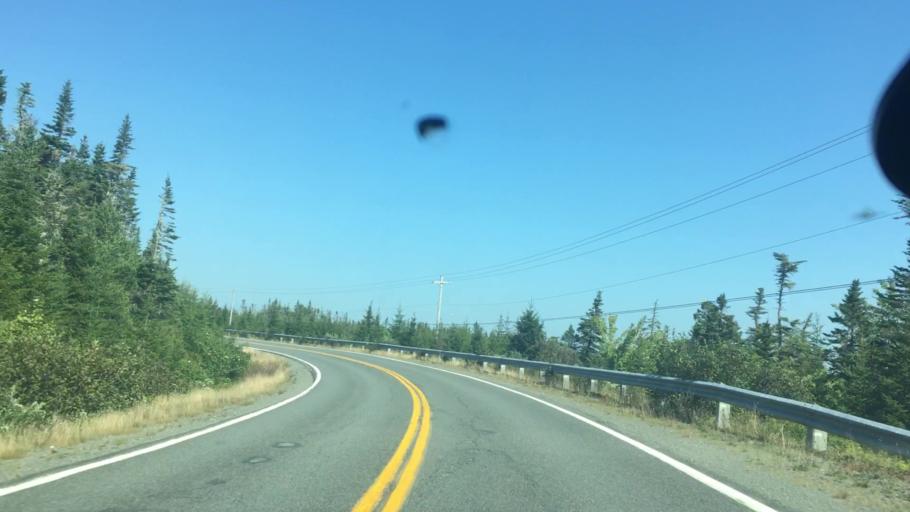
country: CA
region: Nova Scotia
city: Antigonish
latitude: 44.9892
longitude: -62.0957
